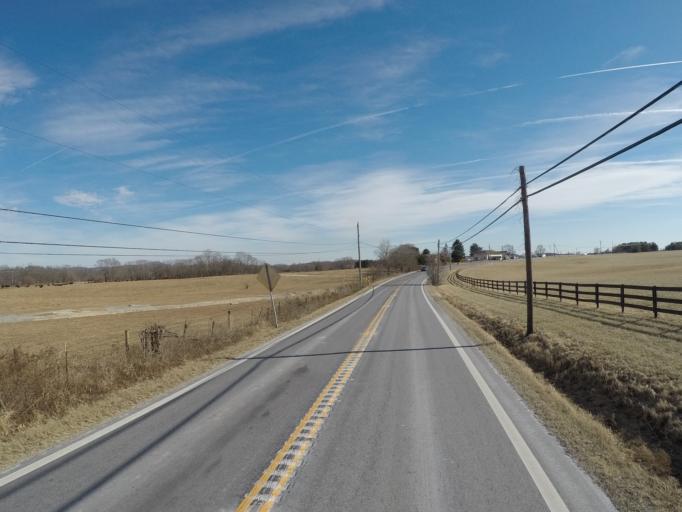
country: US
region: Maryland
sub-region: Frederick County
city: Point of Rocks
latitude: 39.2513
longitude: -77.5323
